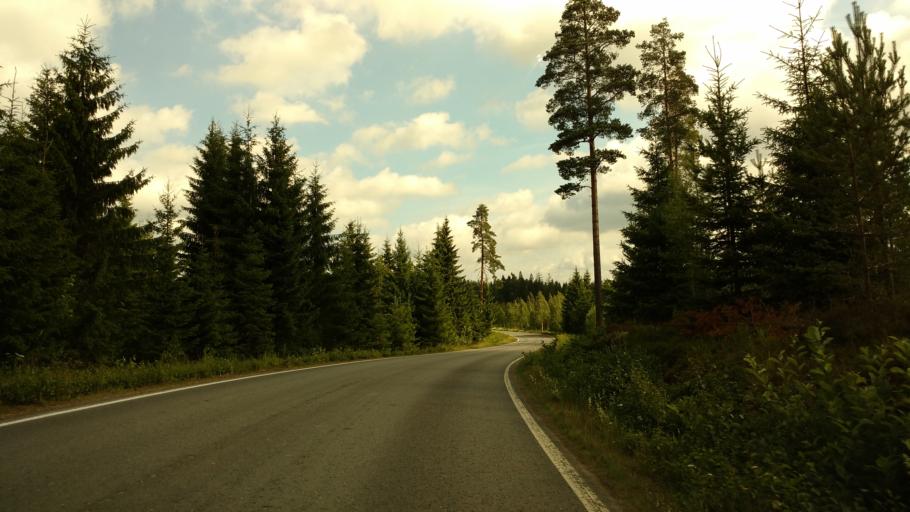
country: FI
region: Haeme
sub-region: Forssa
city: Ypaejae
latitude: 60.7446
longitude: 23.2015
